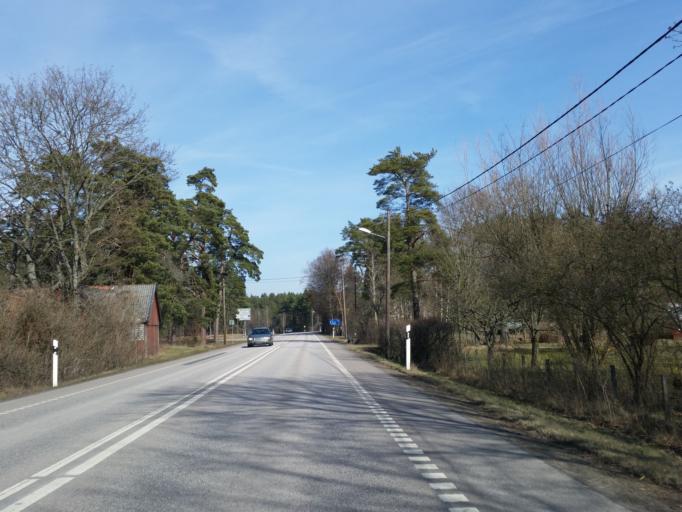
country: SE
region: Kalmar
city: Faerjestaden
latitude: 56.7533
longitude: 16.5524
